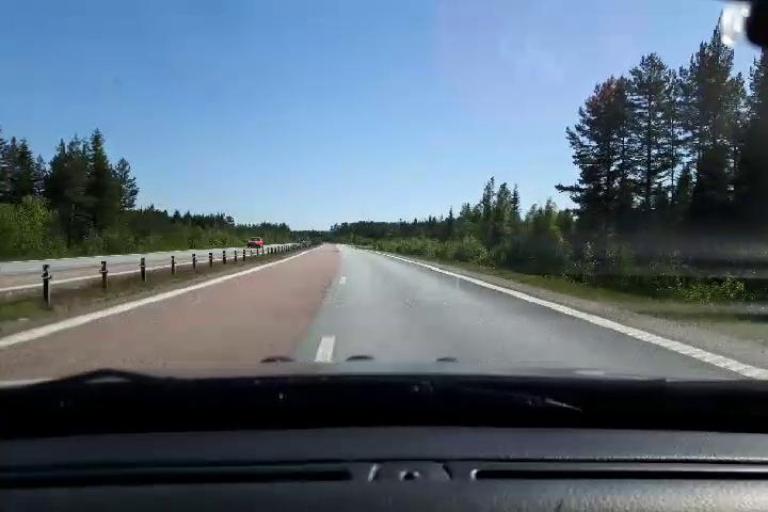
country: SE
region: Gaevleborg
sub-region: Soderhamns Kommun
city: Soderhamn
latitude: 61.4245
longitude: 16.9841
